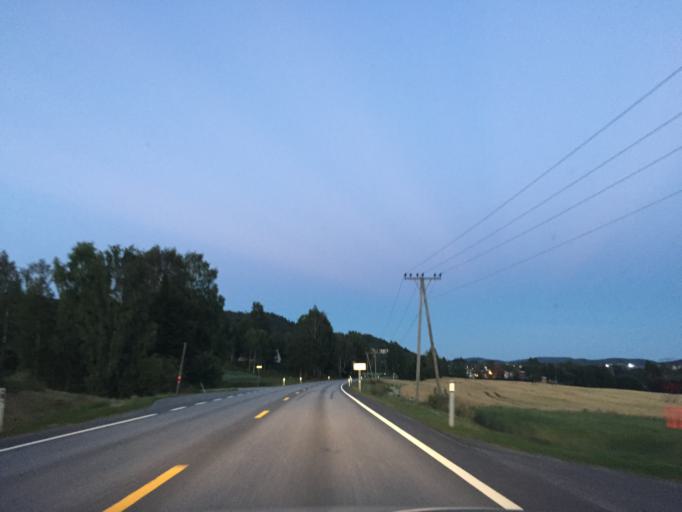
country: NO
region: Hedmark
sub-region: Kongsvinger
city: Kongsvinger
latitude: 60.2124
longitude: 11.9553
